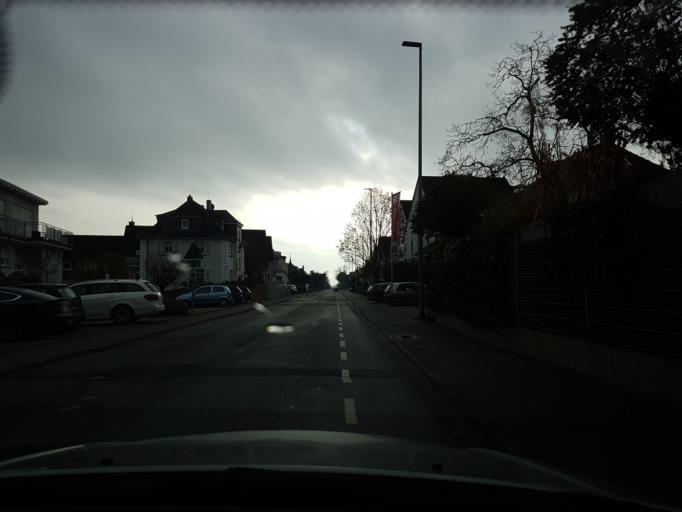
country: DE
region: Hesse
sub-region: Regierungsbezirk Darmstadt
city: Eltville
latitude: 50.0356
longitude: 8.1170
